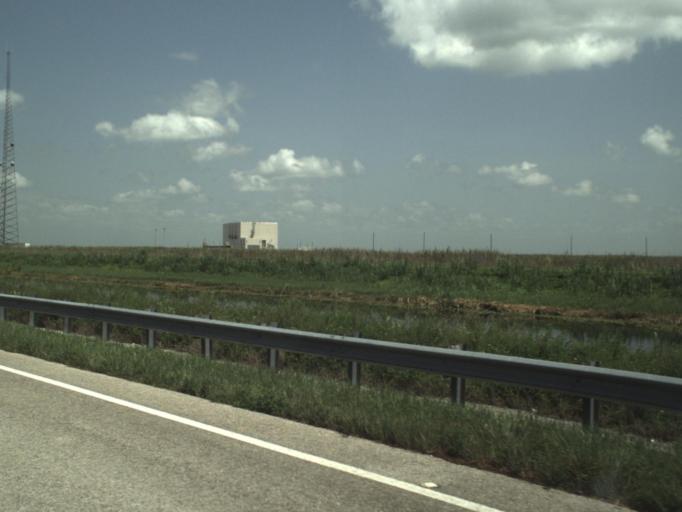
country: US
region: Florida
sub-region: Palm Beach County
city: Belle Glade Camp
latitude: 26.4294
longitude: -80.6107
